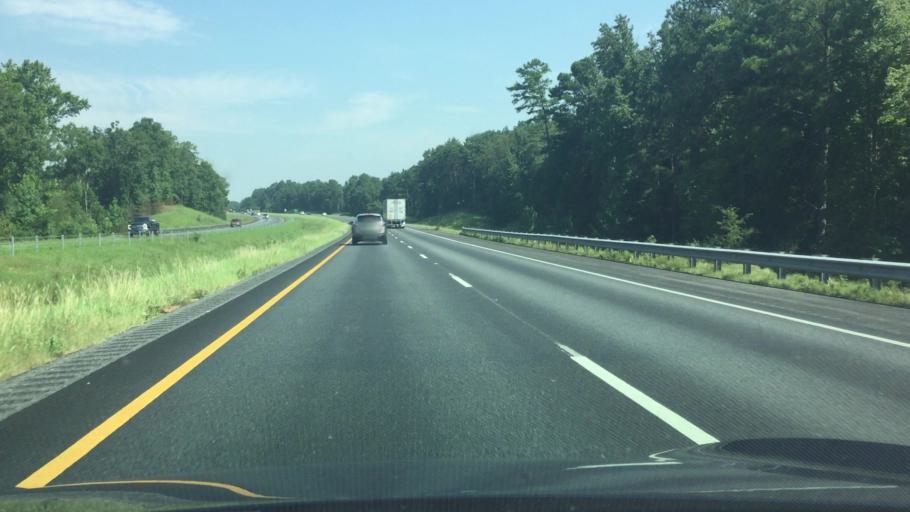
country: US
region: Alabama
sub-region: Shelby County
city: Calera
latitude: 33.0633
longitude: -86.7285
